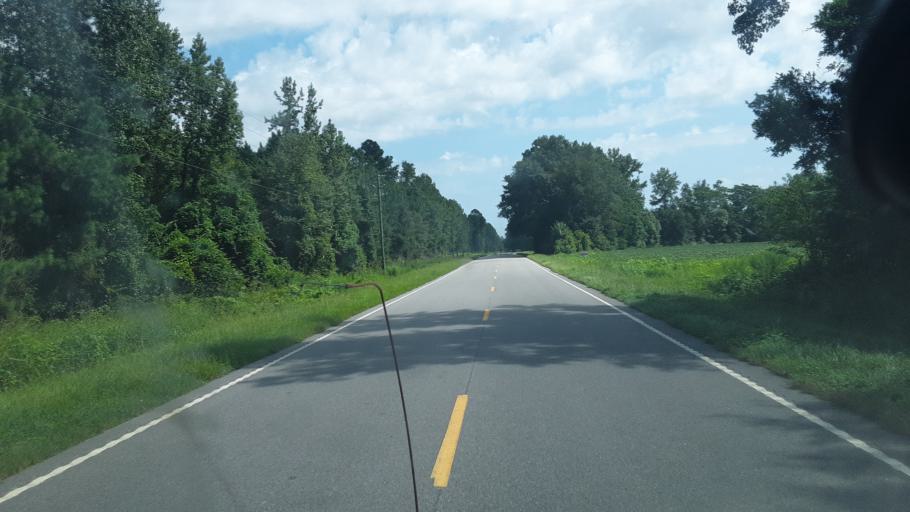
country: US
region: South Carolina
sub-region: Bamberg County
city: Bamberg
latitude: 33.0794
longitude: -81.0224
